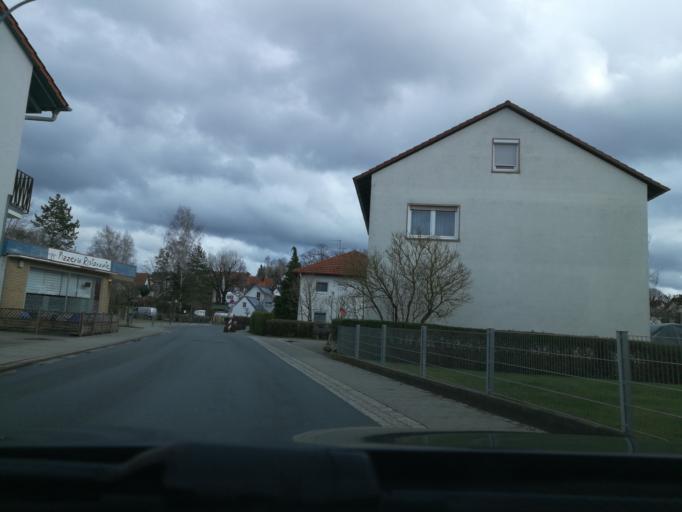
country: DE
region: Bavaria
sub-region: Regierungsbezirk Mittelfranken
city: Rottenbach
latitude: 49.6705
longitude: 10.9285
